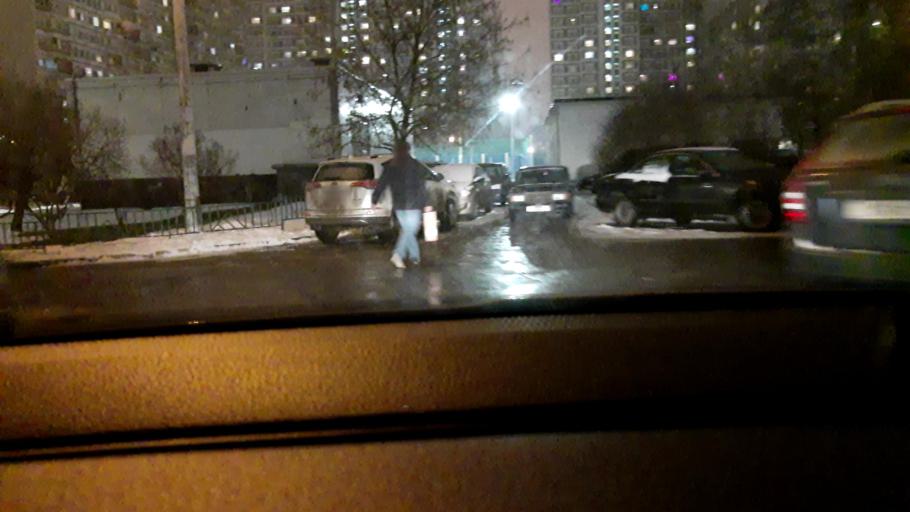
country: RU
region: Moscow
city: Strogino
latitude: 55.7704
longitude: 37.4085
